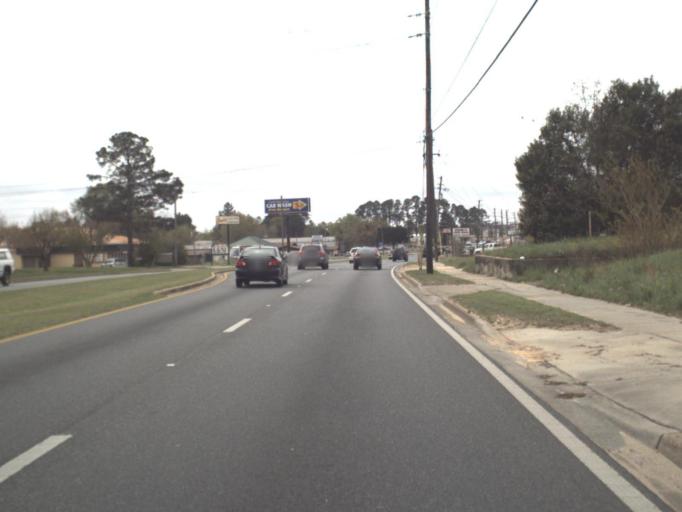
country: US
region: Florida
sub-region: Okaloosa County
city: Crestview
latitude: 30.7428
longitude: -86.5640
